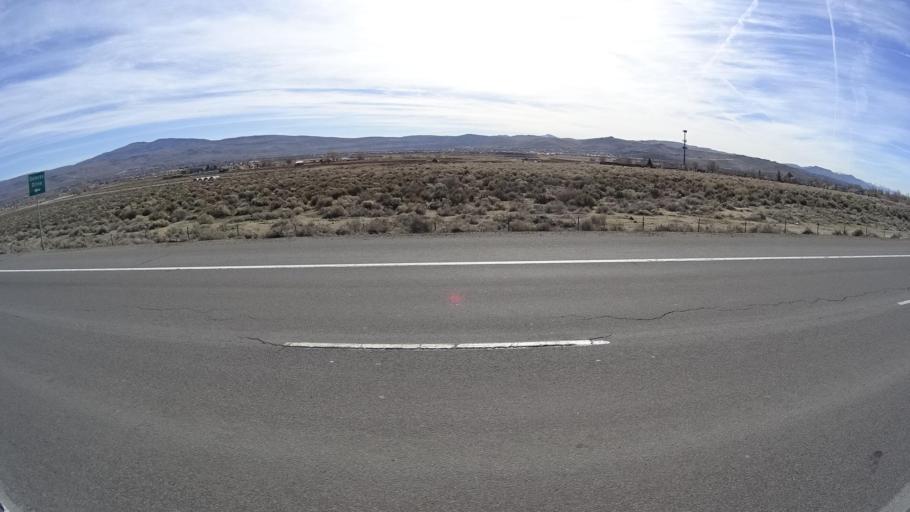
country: US
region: Nevada
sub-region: Washoe County
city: Spanish Springs
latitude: 39.6262
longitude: -119.7197
